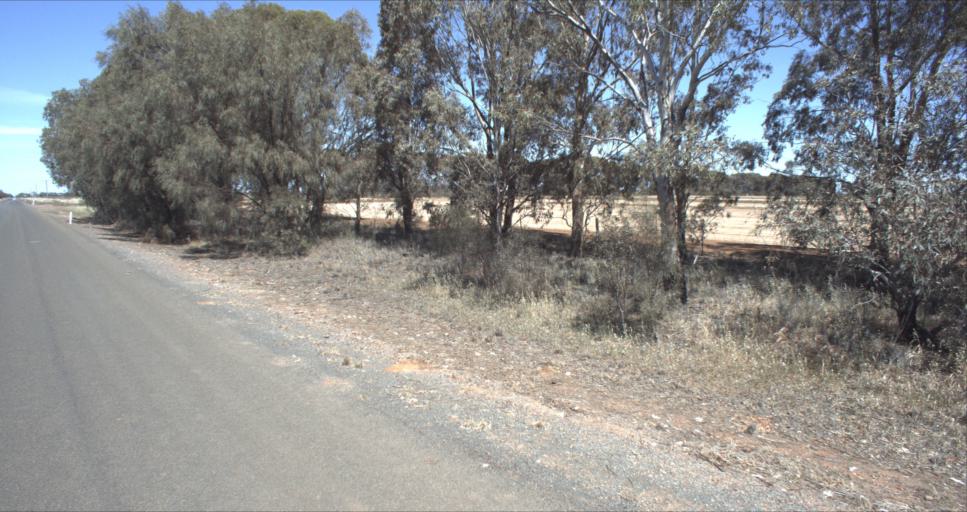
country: AU
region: New South Wales
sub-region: Leeton
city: Leeton
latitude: -34.4722
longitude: 146.2921
